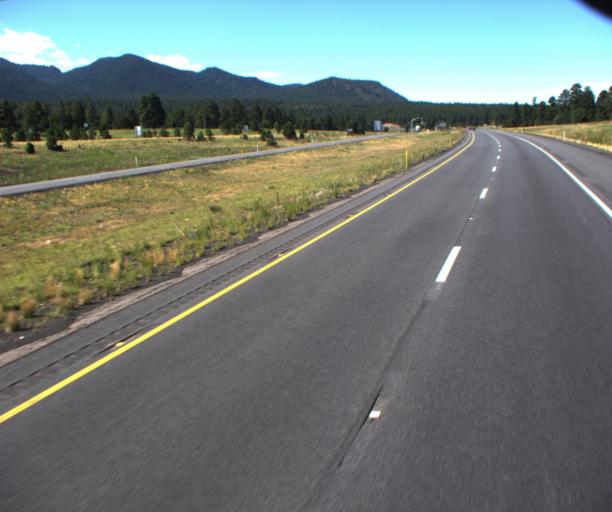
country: US
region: Arizona
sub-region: Coconino County
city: Williams
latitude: 35.2450
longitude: -112.2151
